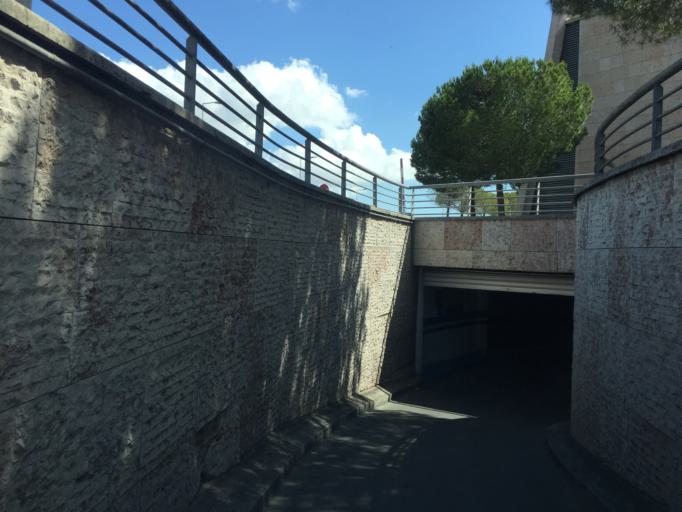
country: PT
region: Setubal
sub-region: Almada
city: Pragal
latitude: 38.6610
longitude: -9.1773
